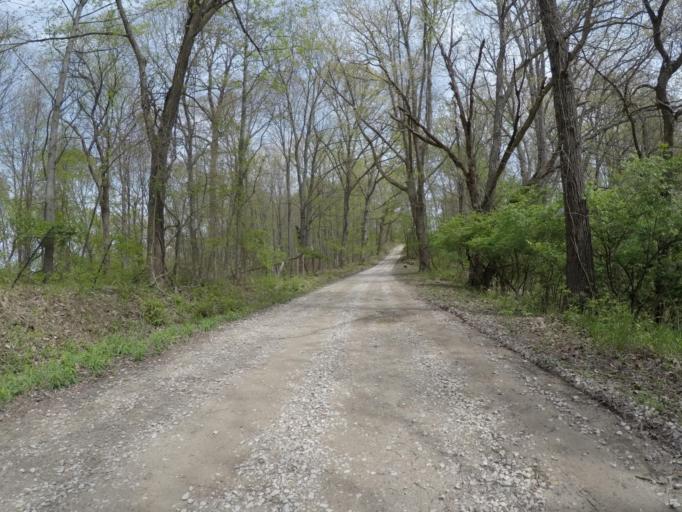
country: US
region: West Virginia
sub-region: Wayne County
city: Lavalette
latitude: 38.3679
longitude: -82.4814
